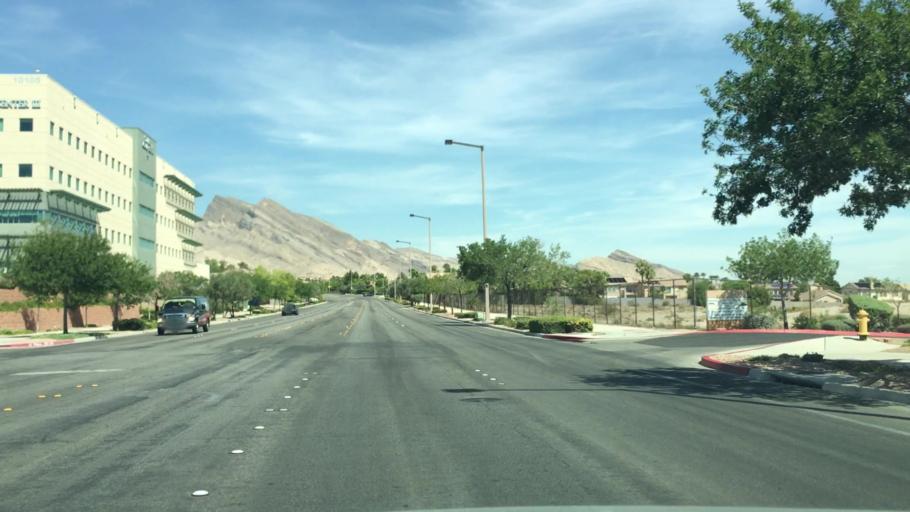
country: US
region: Nevada
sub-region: Clark County
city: Summerlin South
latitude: 36.1823
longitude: -115.3152
